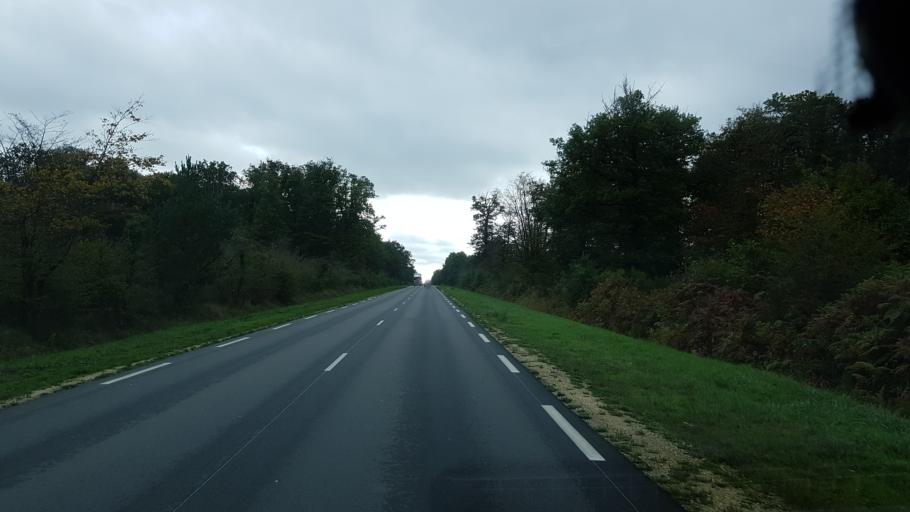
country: FR
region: Centre
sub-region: Departement du Loir-et-Cher
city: Theillay
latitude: 47.2674
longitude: 2.0597
